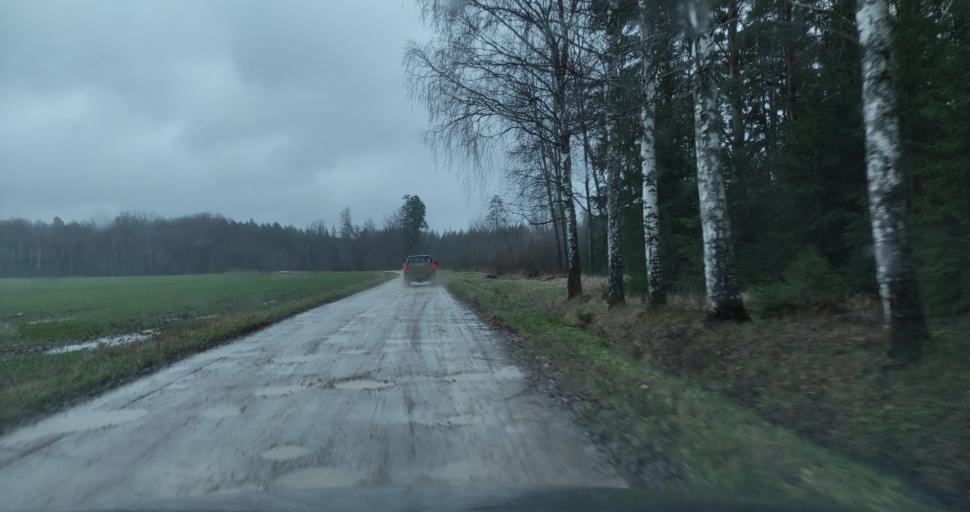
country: LV
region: Skrunda
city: Skrunda
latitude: 56.6022
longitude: 22.1197
